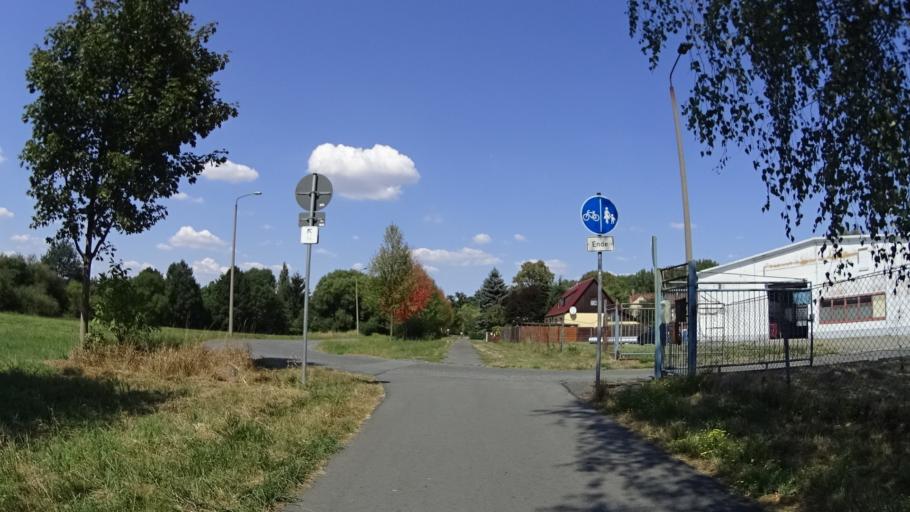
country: DE
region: Saxony
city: Zittau
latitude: 50.8949
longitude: 14.8326
